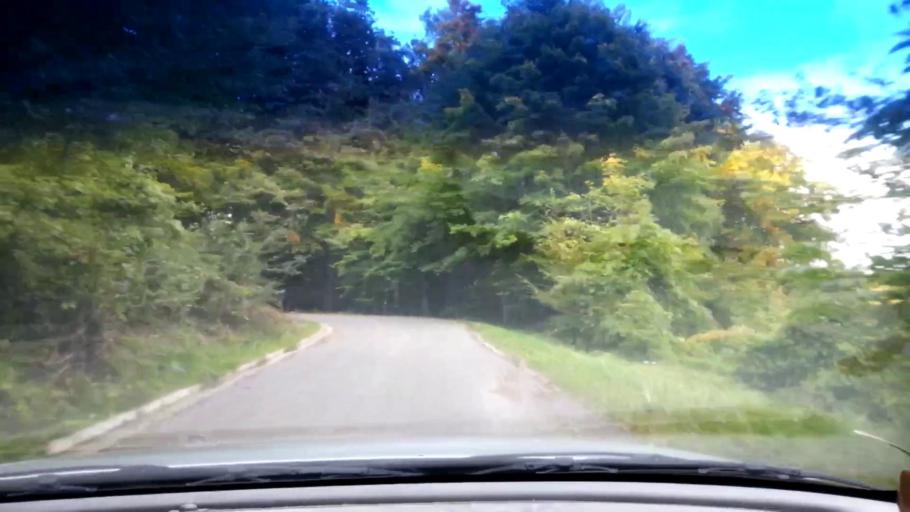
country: DE
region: Bavaria
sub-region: Upper Franconia
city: Schesslitz
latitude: 49.9910
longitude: 11.0763
